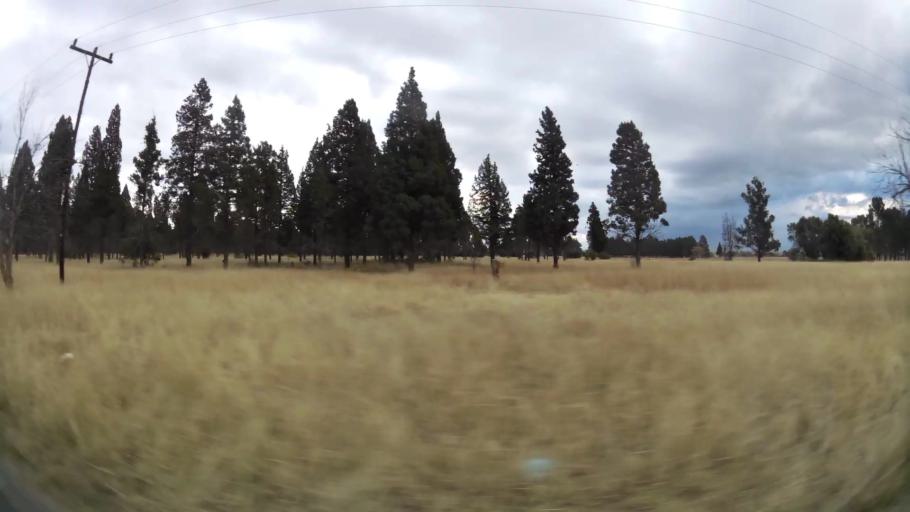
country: ZA
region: Orange Free State
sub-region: Lejweleputswa District Municipality
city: Welkom
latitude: -27.9718
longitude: 26.7006
